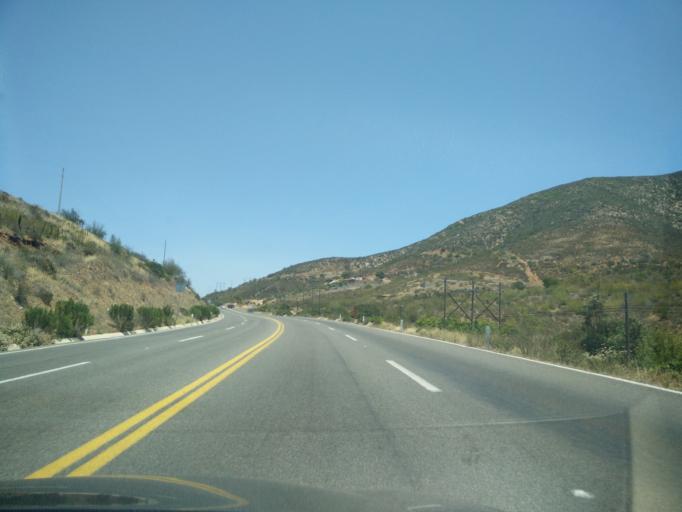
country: MX
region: Baja California
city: El Sauzal
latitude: 31.9564
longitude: -116.6629
